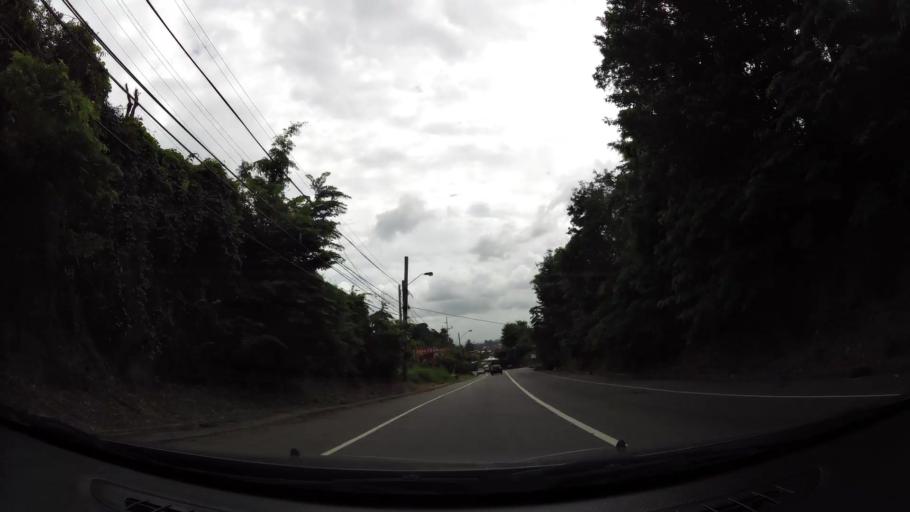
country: TT
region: San Juan/Laventille
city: Laventille
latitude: 10.6677
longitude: -61.4844
